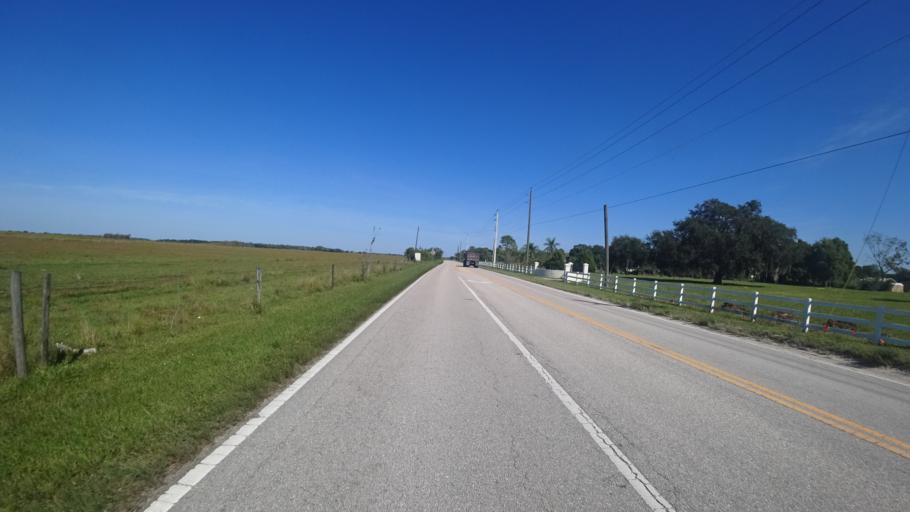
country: US
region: Florida
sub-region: Sarasota County
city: Lake Sarasota
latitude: 27.3391
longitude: -82.2694
